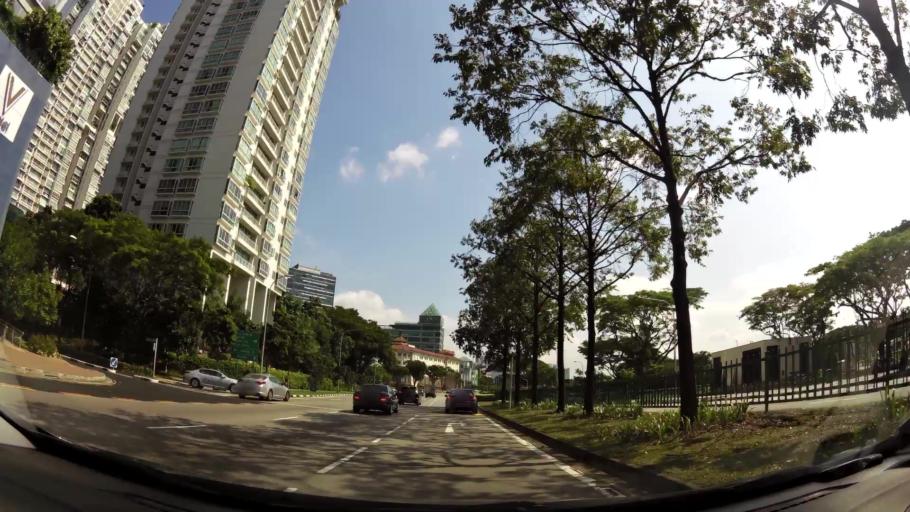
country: SG
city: Singapore
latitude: 1.3077
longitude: 103.8631
